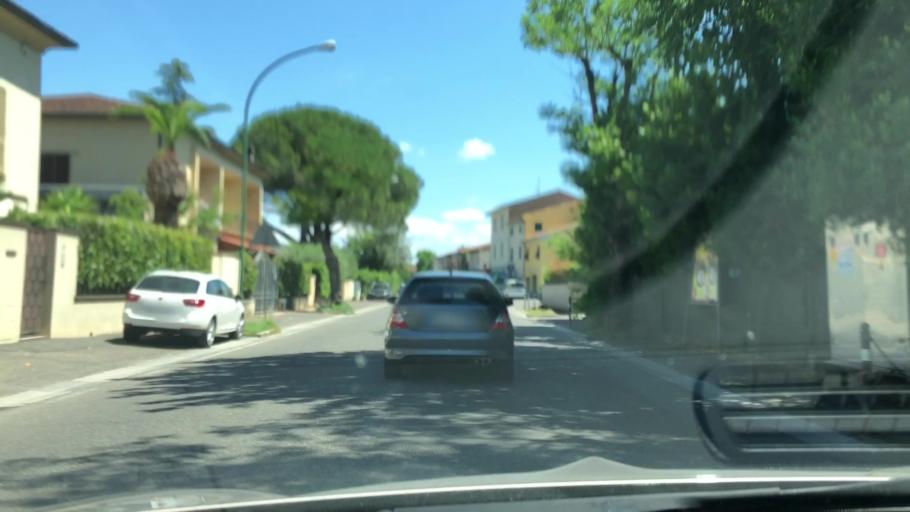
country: IT
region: Tuscany
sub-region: Province of Pisa
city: Ponsacco
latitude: 43.6188
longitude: 10.6355
